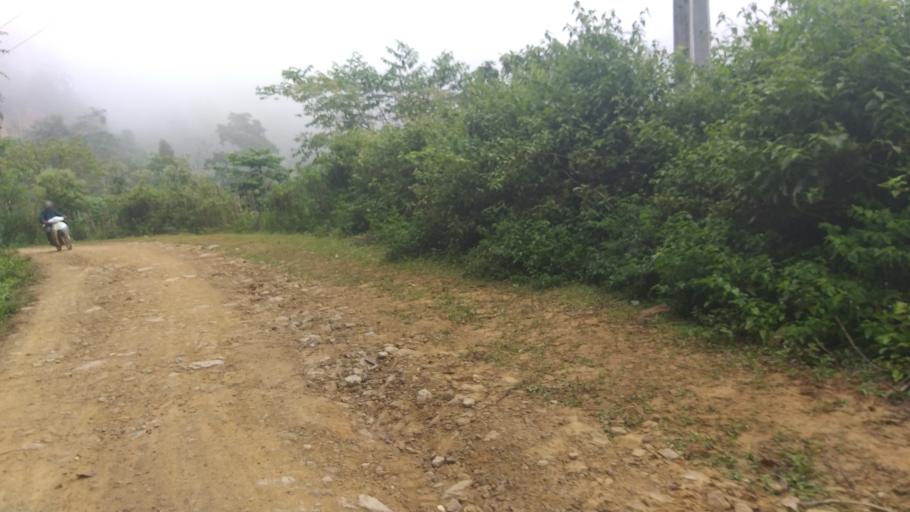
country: LA
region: Phongsali
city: Khoa
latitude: 21.2554
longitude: 102.6641
